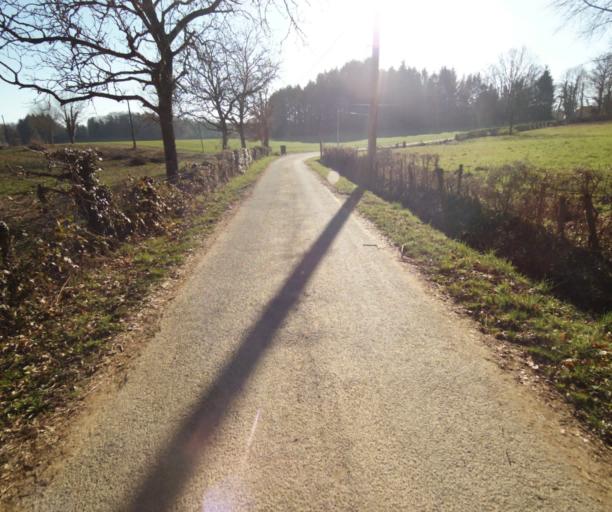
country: FR
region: Limousin
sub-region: Departement de la Correze
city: Uzerche
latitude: 45.3875
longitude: 1.6221
